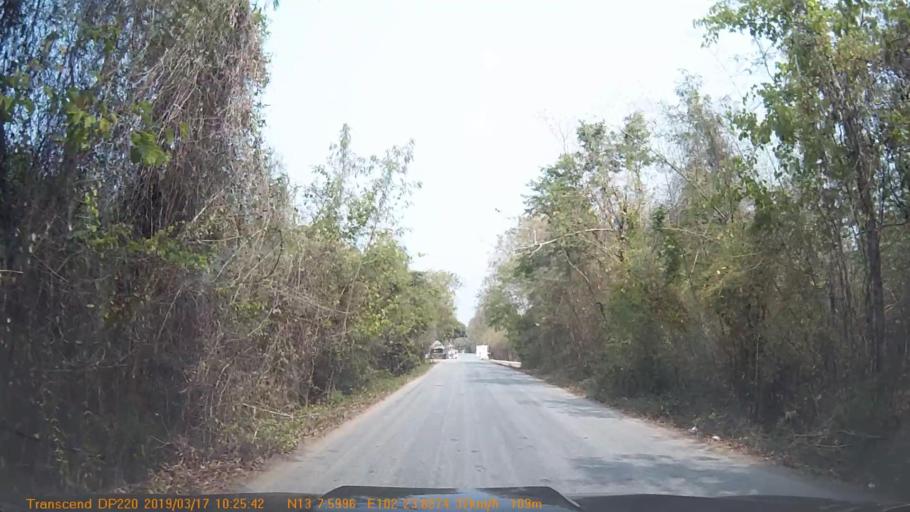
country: TH
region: Chanthaburi
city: Soi Dao
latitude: 13.1267
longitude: 102.3971
